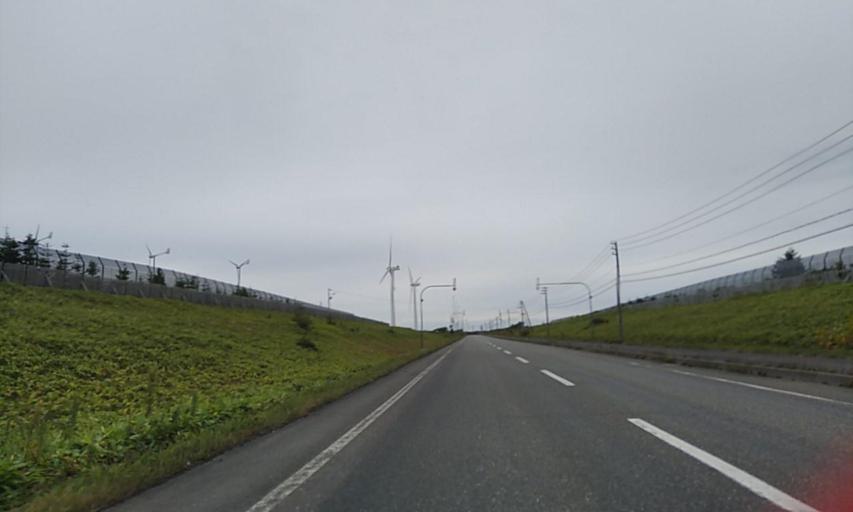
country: JP
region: Hokkaido
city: Makubetsu
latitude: 45.2880
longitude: 142.2159
